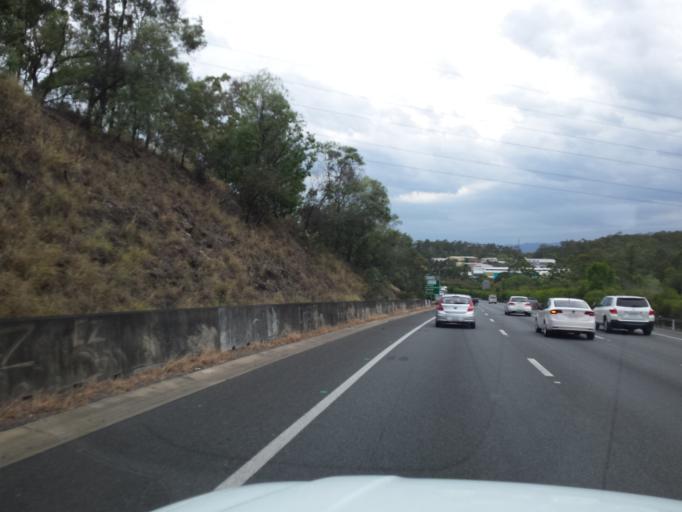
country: AU
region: Queensland
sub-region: Gold Coast
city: Nerang
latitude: -27.9765
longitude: 153.3450
